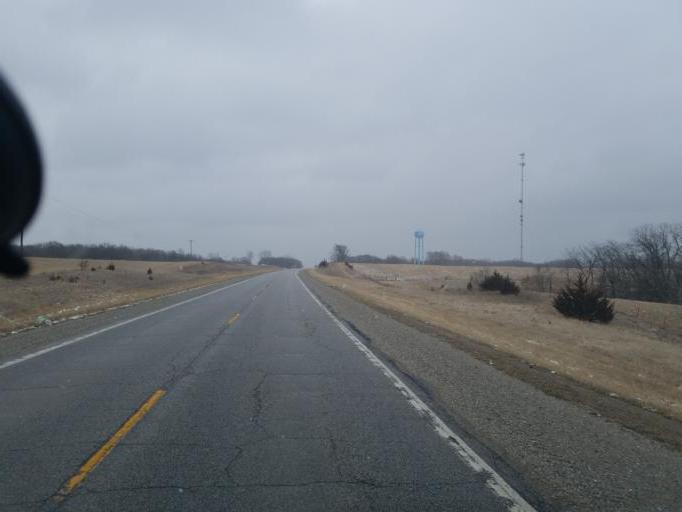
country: US
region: Missouri
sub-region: Putnam County
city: Unionville
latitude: 40.4706
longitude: -92.8174
